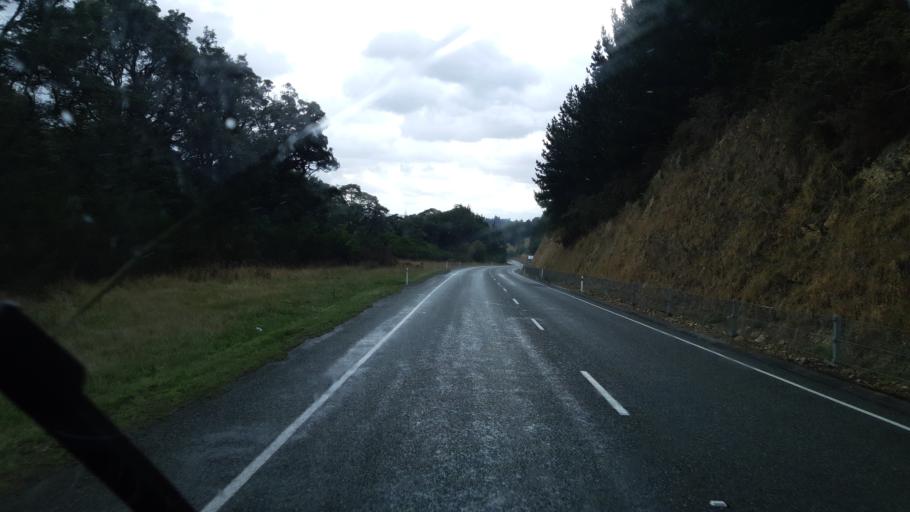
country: NZ
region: Tasman
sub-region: Tasman District
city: Wakefield
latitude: -41.4769
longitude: 172.9316
